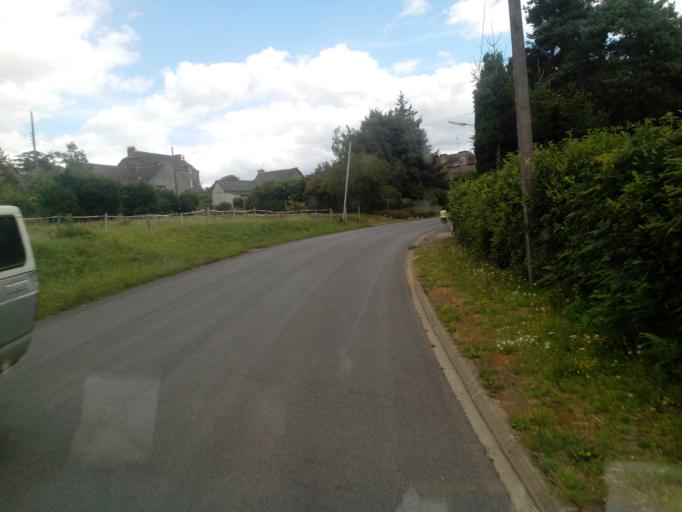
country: FR
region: Brittany
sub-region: Departement du Morbihan
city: Guilliers
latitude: 48.0800
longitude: -2.4139
